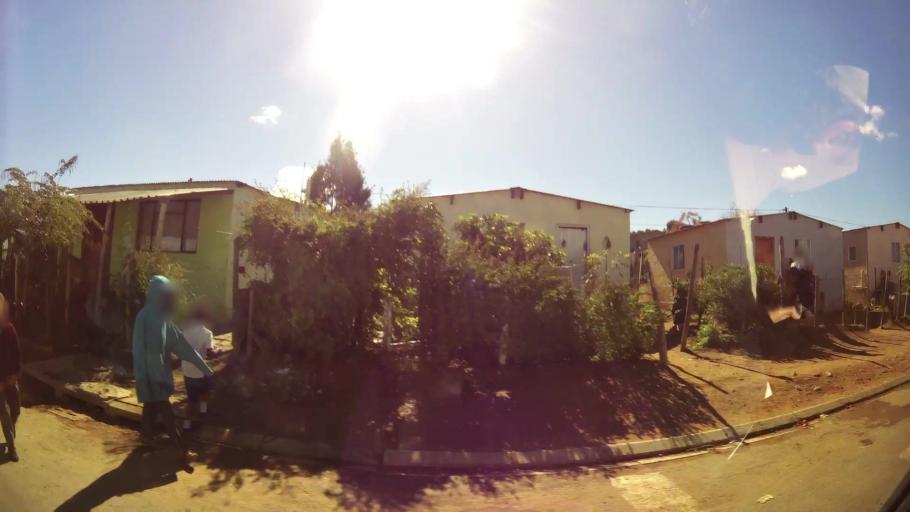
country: ZA
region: Western Cape
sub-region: Cape Winelands District Municipality
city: Ashton
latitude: -33.8315
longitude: 20.0474
